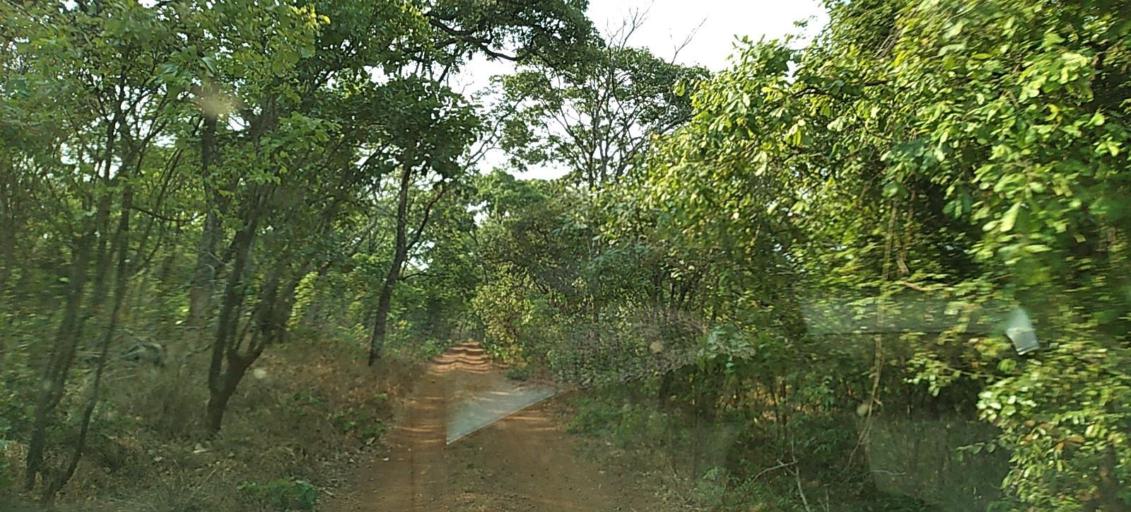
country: ZM
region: Copperbelt
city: Kalulushi
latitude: -12.9793
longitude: 27.7173
